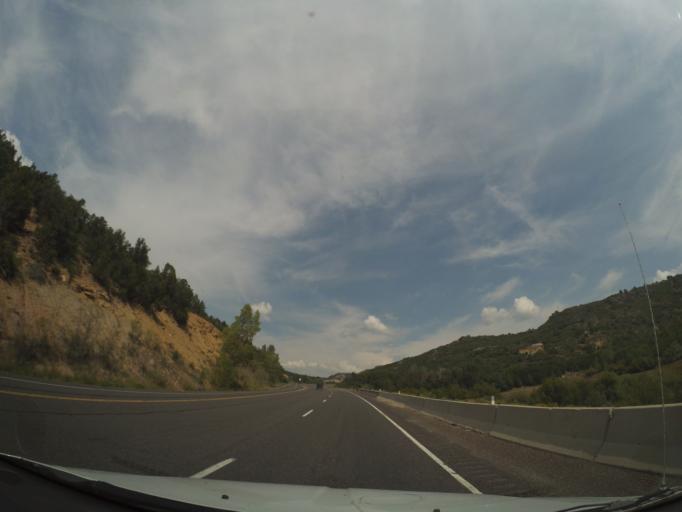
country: US
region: Utah
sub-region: Garfield County
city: Panguitch
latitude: 37.6227
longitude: -112.1729
